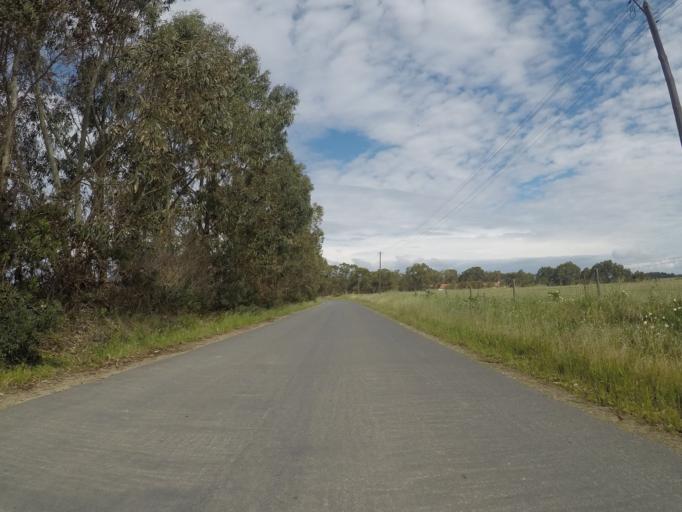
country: PT
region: Beja
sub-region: Odemira
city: Sao Teotonio
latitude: 37.4937
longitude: -8.7842
